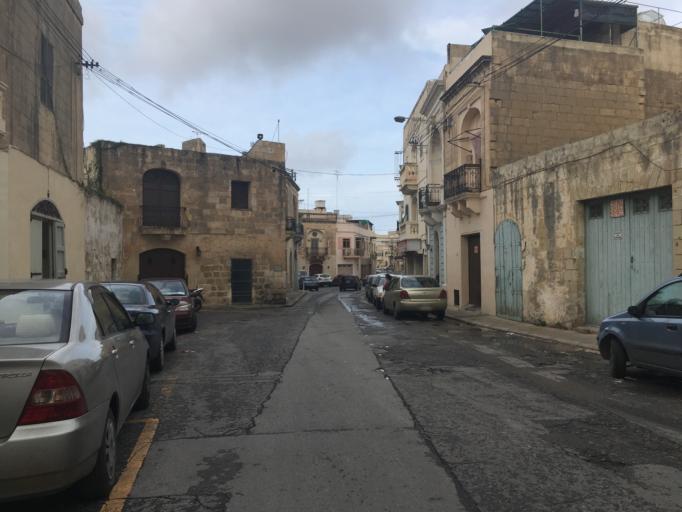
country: MT
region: Il-Mosta
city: Mosta
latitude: 35.9100
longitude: 14.4269
